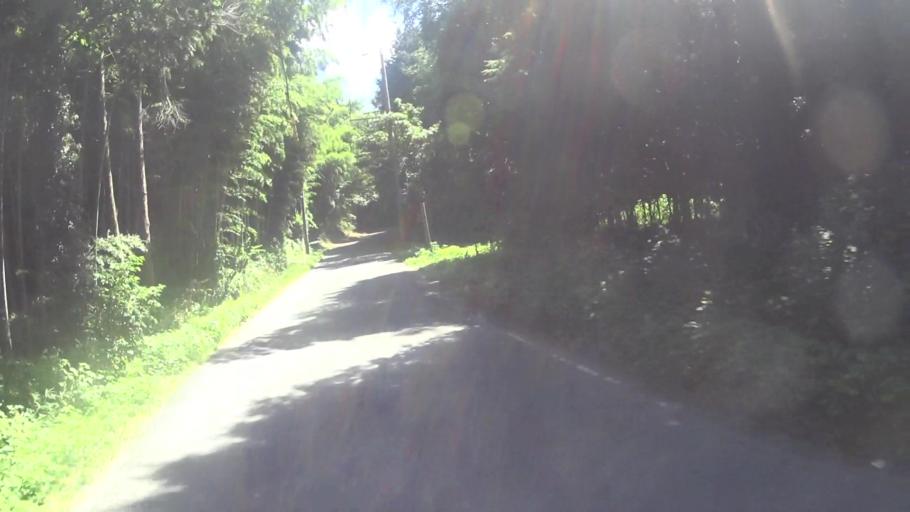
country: JP
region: Nara
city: Nara-shi
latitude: 34.7688
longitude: 135.8726
